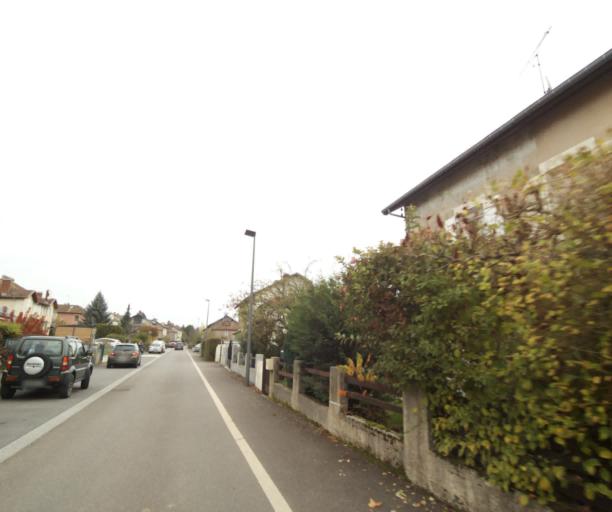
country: FR
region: Lorraine
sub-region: Departement de Meurthe-et-Moselle
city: Mancieulles
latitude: 49.2859
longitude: 5.8978
